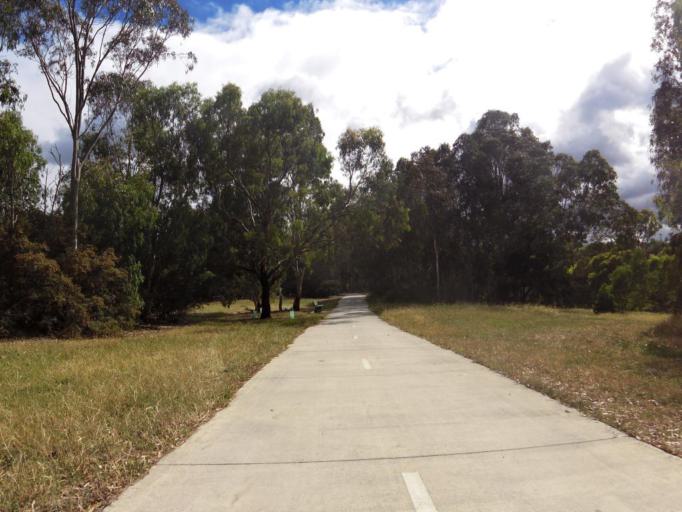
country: AU
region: Victoria
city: Heidelberg West
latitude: -37.7605
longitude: 145.0286
